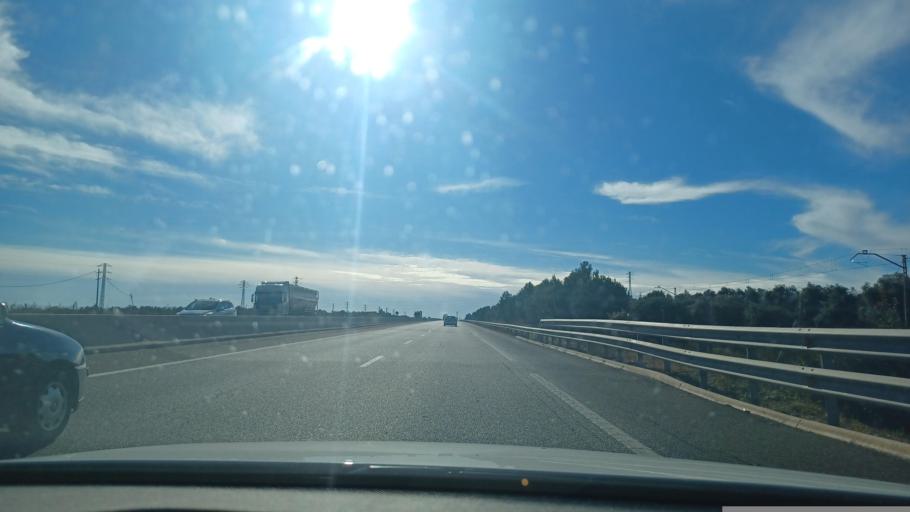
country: ES
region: Catalonia
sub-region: Provincia de Tarragona
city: Alcover
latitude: 41.2347
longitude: 1.1643
